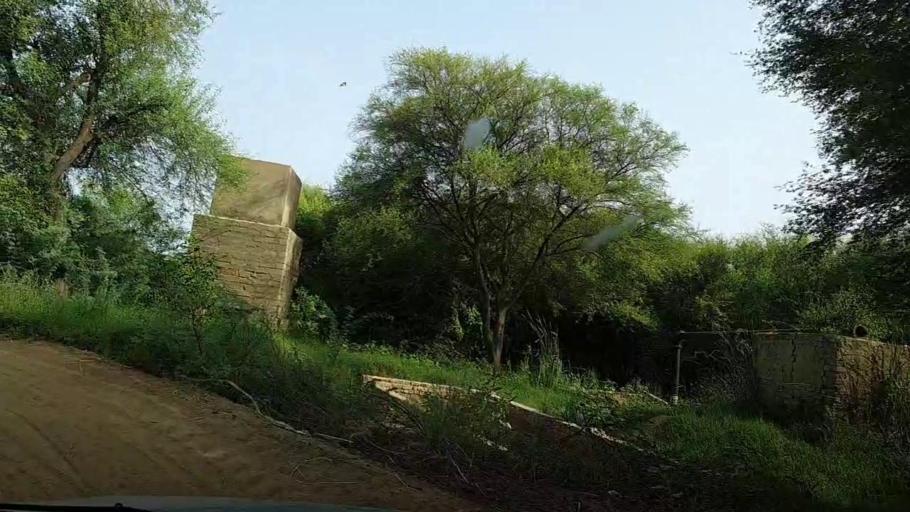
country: PK
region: Sindh
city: Kotri
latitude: 25.2353
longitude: 68.2464
